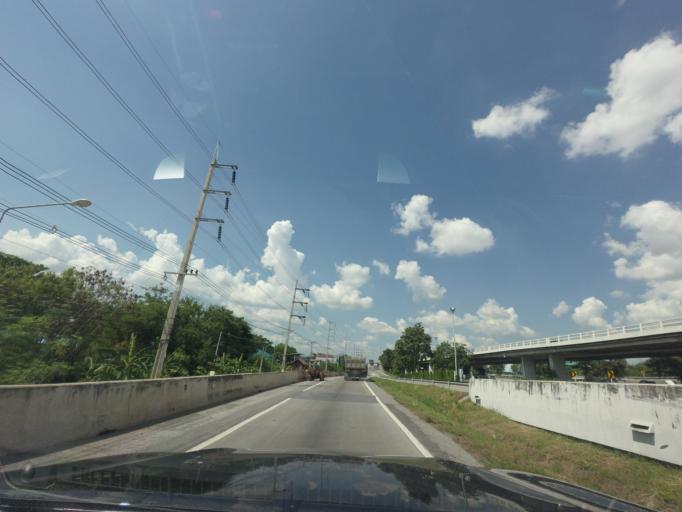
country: TH
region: Nakhon Ratchasima
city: Nakhon Ratchasima
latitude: 14.9614
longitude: 102.0528
